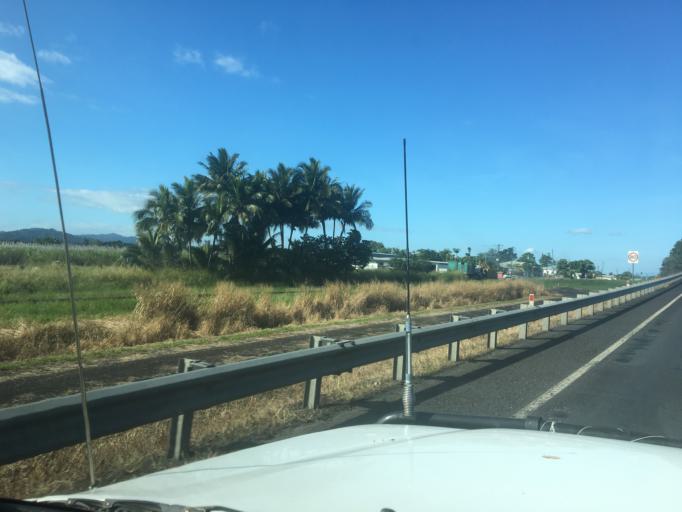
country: AU
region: Queensland
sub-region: Cassowary Coast
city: Innisfail
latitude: -17.3313
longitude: 145.9281
